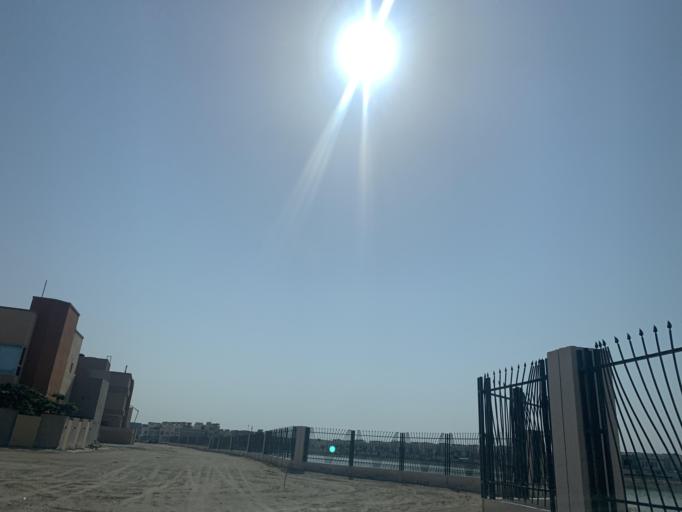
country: BH
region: Central Governorate
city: Madinat Hamad
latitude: 26.1322
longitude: 50.4862
